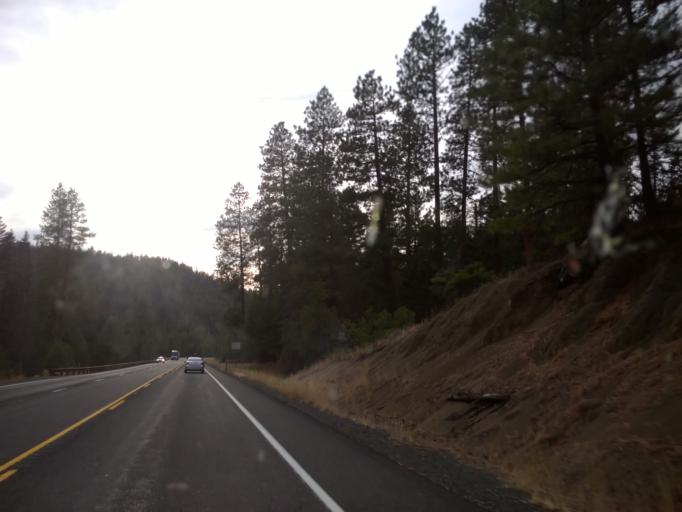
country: US
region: Washington
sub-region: Chelan County
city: Cashmere
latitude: 47.3316
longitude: -120.6072
